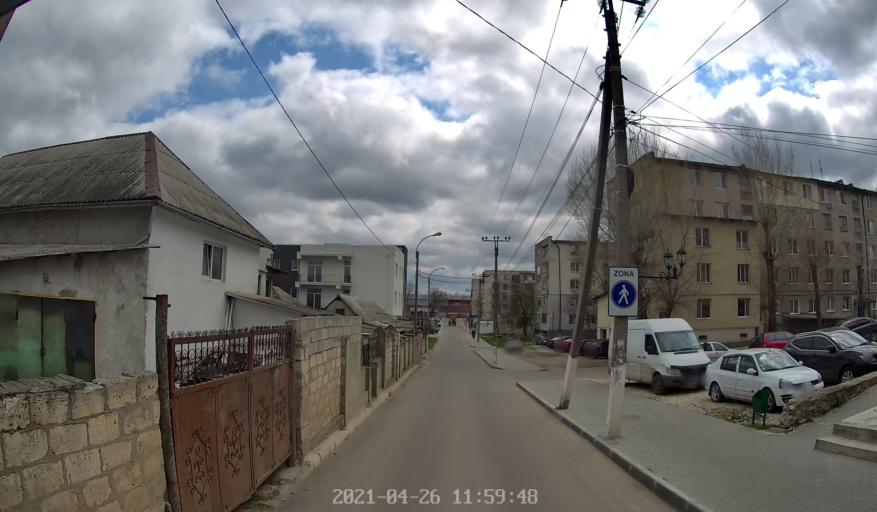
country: MD
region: Chisinau
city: Ciorescu
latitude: 47.1278
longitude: 28.8888
